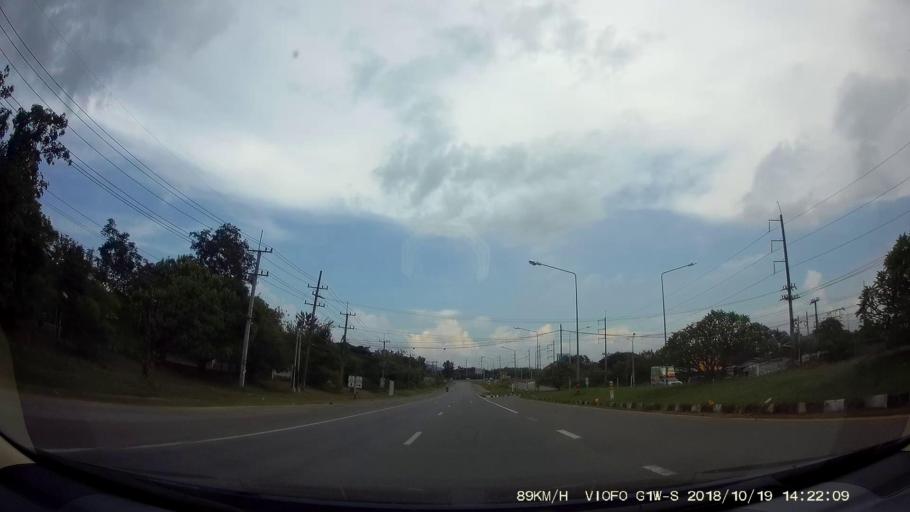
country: TH
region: Chaiyaphum
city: Kaeng Khro
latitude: 16.0598
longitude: 102.2730
